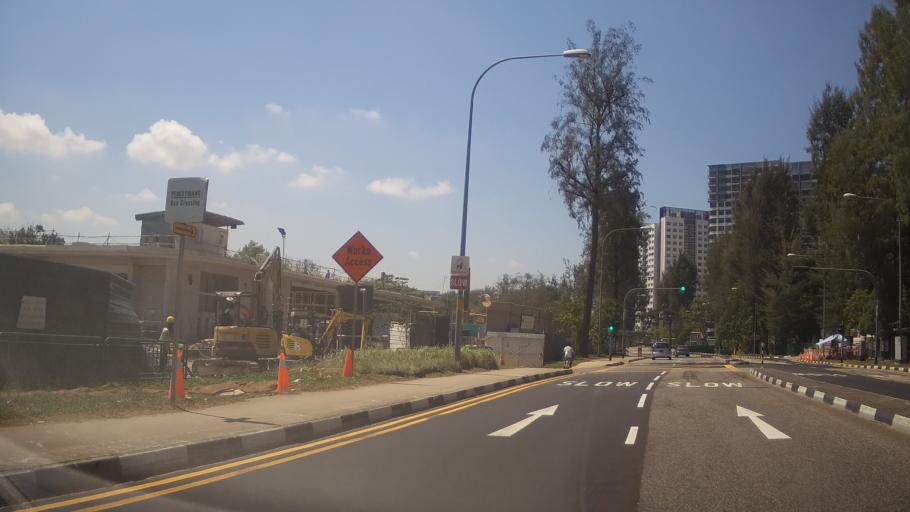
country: SG
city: Singapore
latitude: 1.3310
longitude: 103.7249
